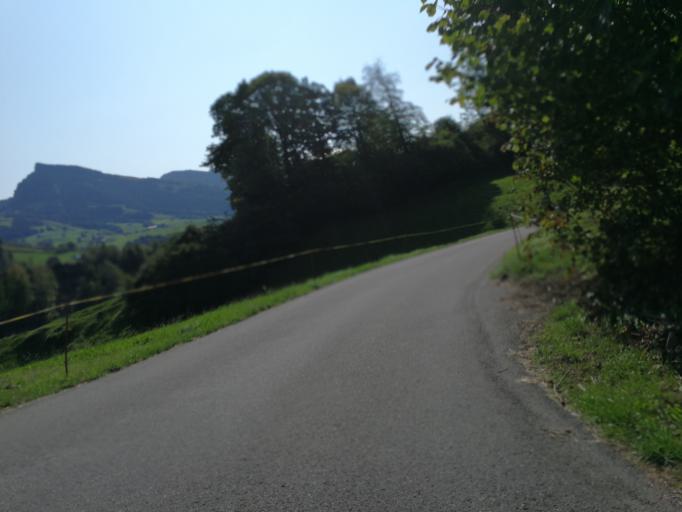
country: CH
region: Saint Gallen
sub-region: Wahlkreis Toggenburg
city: Krummenau
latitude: 47.2371
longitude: 9.1802
